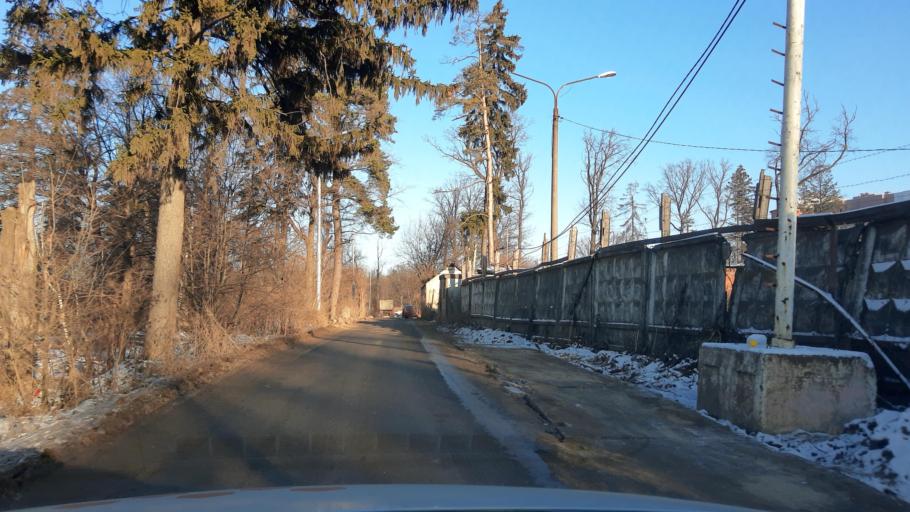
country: RU
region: Moskovskaya
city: Mosrentgen
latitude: 55.6054
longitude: 37.4675
